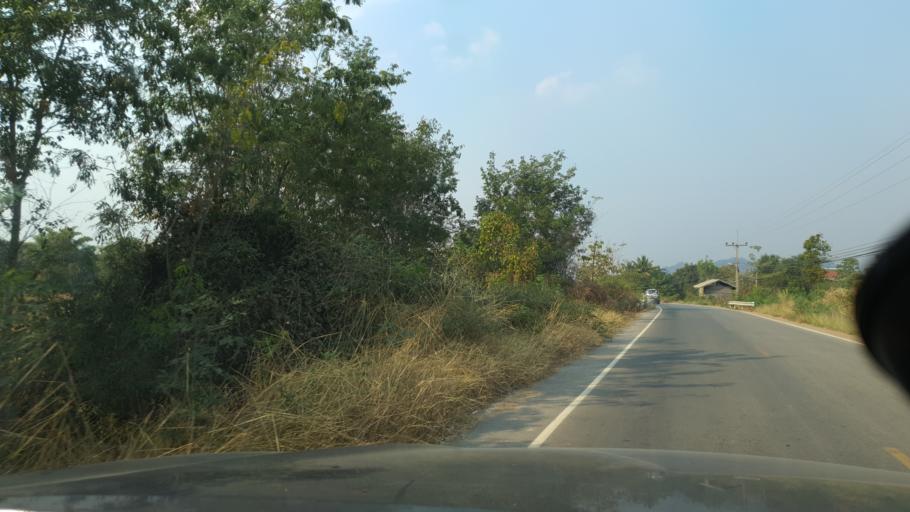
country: TH
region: Sukhothai
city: Ban Dan Lan Hoi
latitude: 17.1088
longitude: 99.5507
